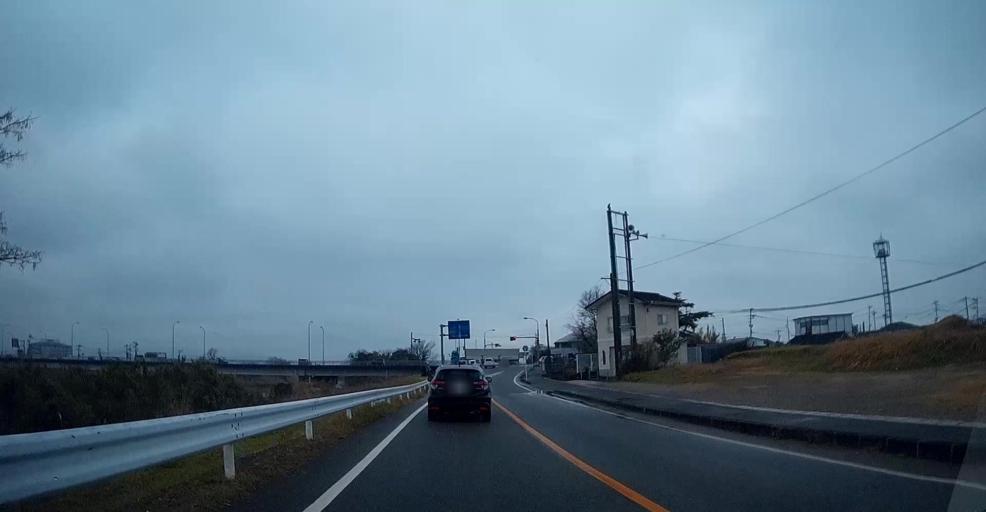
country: JP
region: Kumamoto
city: Kumamoto
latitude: 32.7536
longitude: 130.7388
